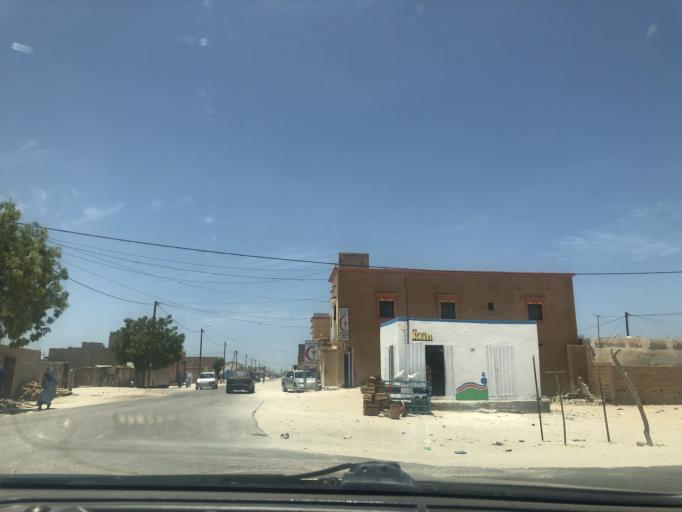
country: MR
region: Nouakchott
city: Nouakchott
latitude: 18.0027
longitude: -15.9673
